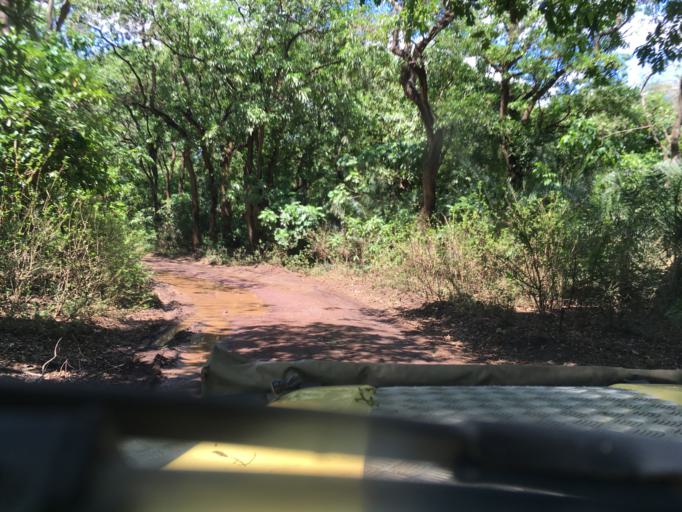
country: TZ
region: Arusha
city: Mto wa Mbu
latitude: -3.4100
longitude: 35.8211
